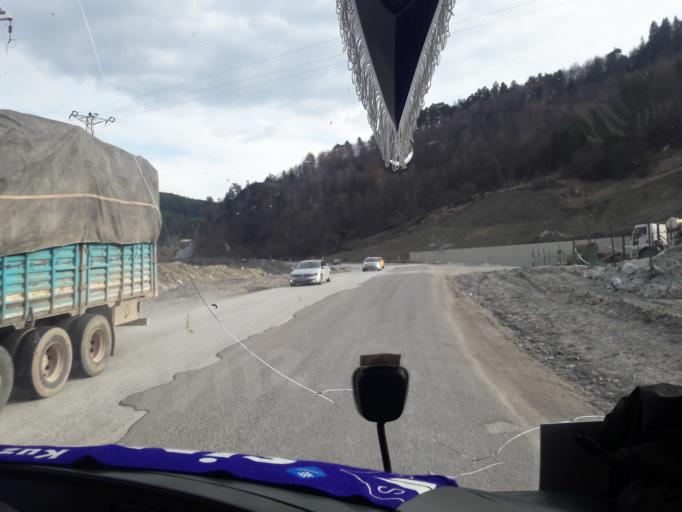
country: TR
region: Kastamonu
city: Kuzyaka
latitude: 41.1115
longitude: 33.7503
